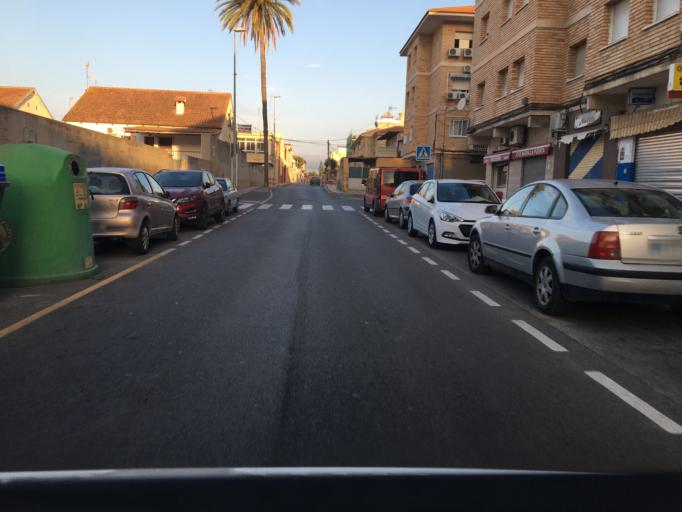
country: ES
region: Murcia
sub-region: Murcia
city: Cartagena
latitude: 37.6239
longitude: -0.9856
